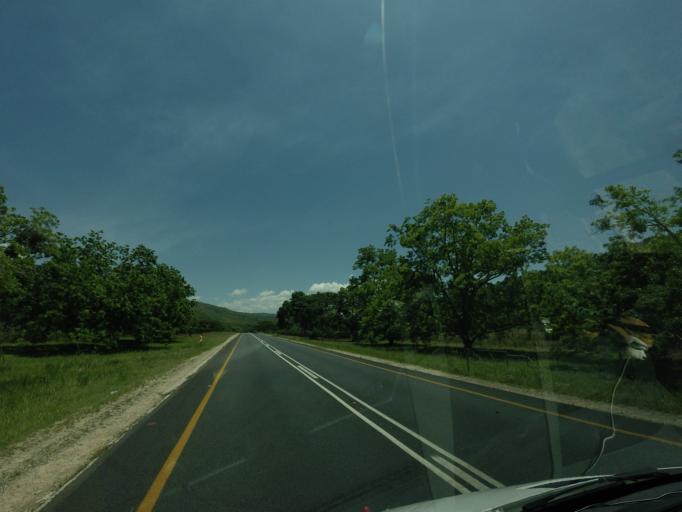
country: ZA
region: Mpumalanga
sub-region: Ehlanzeni District
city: Nelspruit
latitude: -25.4343
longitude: 30.6460
